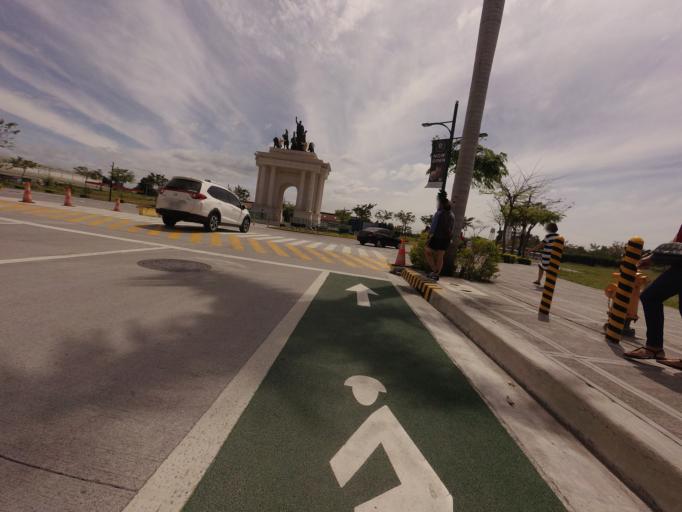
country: PH
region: Metro Manila
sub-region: Pasig
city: Pasig City
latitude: 14.5777
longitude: 121.0756
